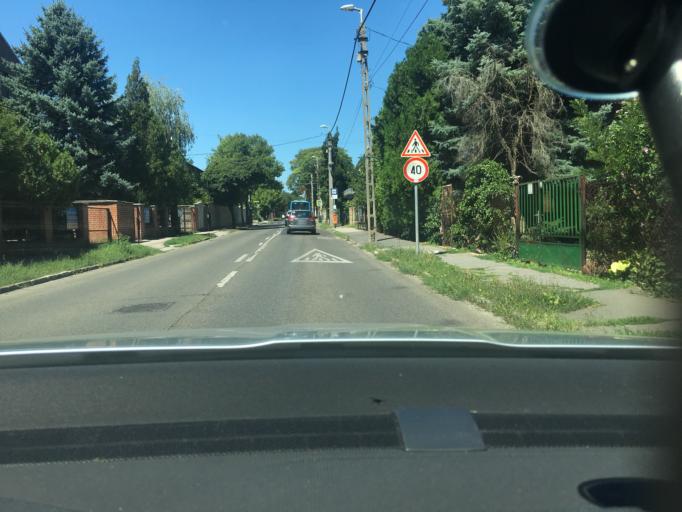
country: HU
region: Budapest
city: Budapest XVI. keruelet
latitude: 47.5110
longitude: 19.1773
